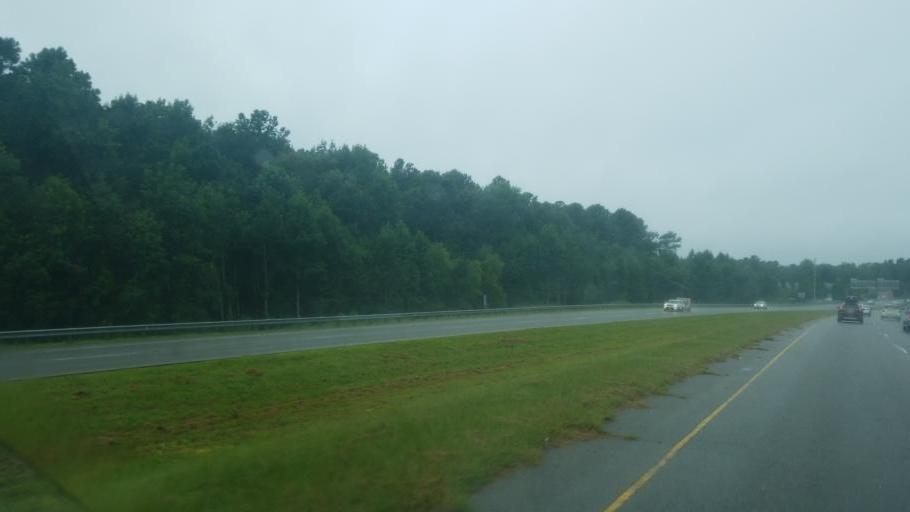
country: US
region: Virginia
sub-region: City of Chesapeake
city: Chesapeake
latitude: 36.7372
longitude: -76.2428
